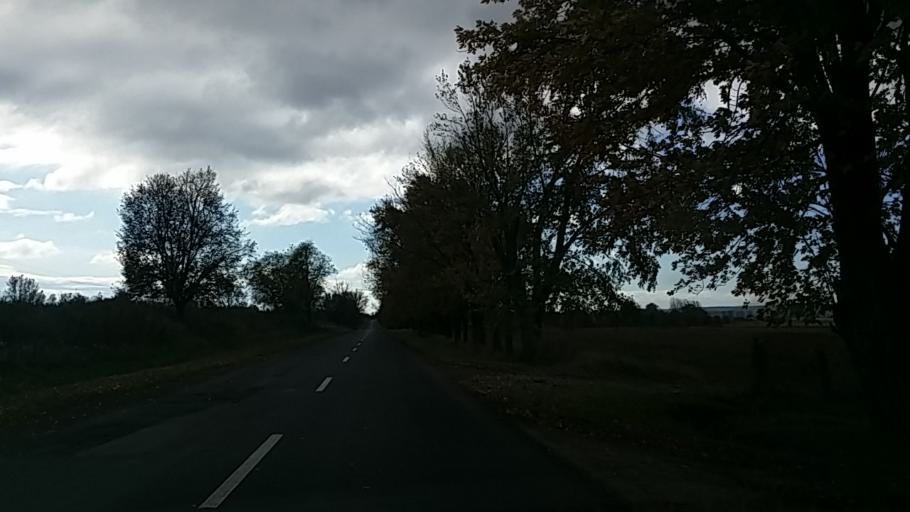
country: HU
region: Borsod-Abauj-Zemplen
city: Gonc
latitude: 48.4609
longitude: 21.2478
